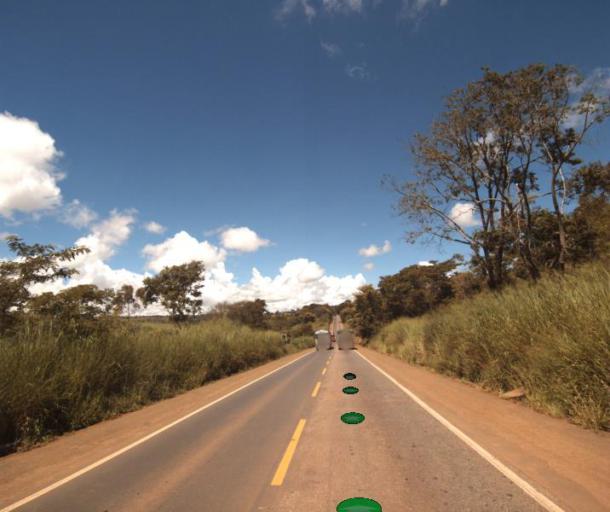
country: BR
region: Goias
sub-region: Anapolis
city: Anapolis
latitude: -16.1630
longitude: -49.0434
